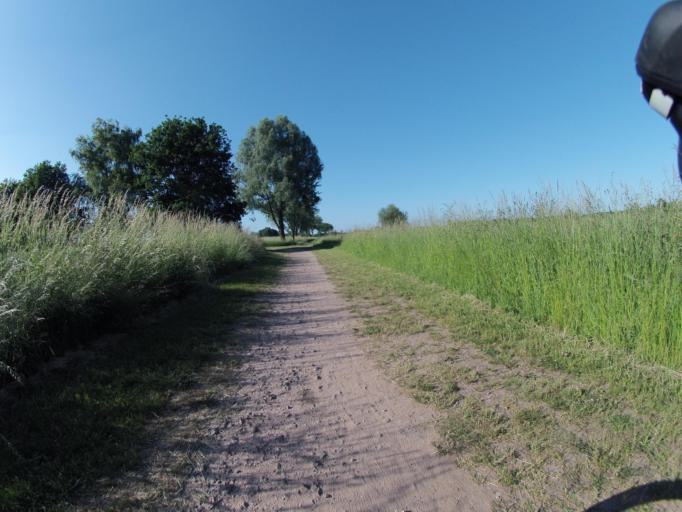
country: DE
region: Lower Saxony
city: Suddendorf
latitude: 52.3095
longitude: 7.2326
